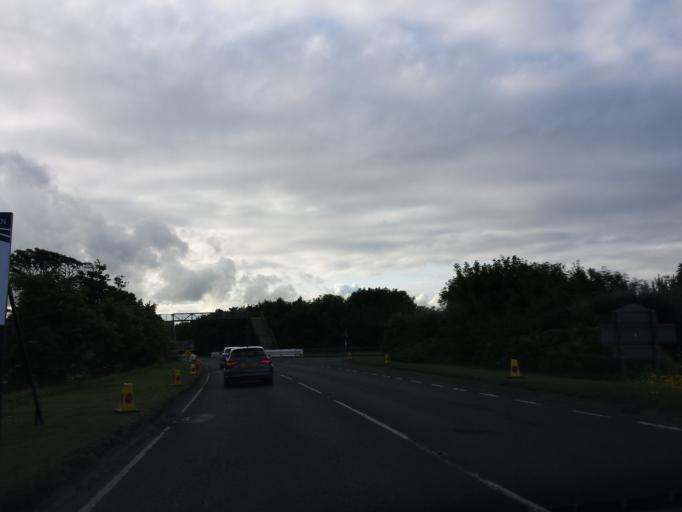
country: GB
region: Scotland
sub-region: Fife
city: Saint Andrews
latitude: 56.3454
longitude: -2.8185
